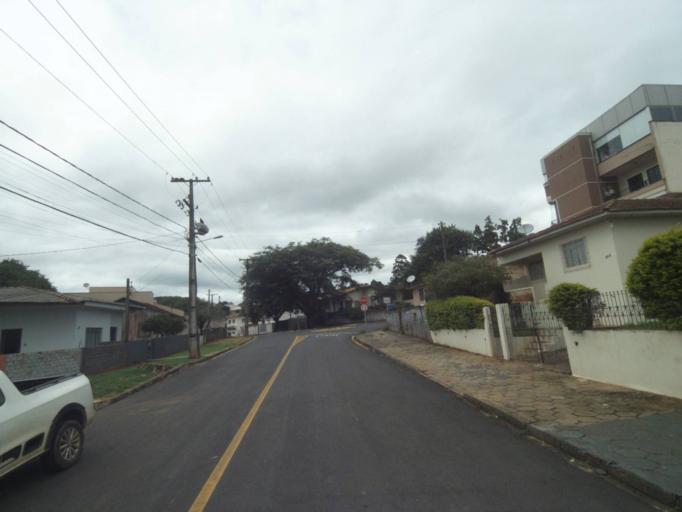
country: BR
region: Parana
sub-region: Telemaco Borba
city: Telemaco Borba
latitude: -24.3277
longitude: -50.6140
